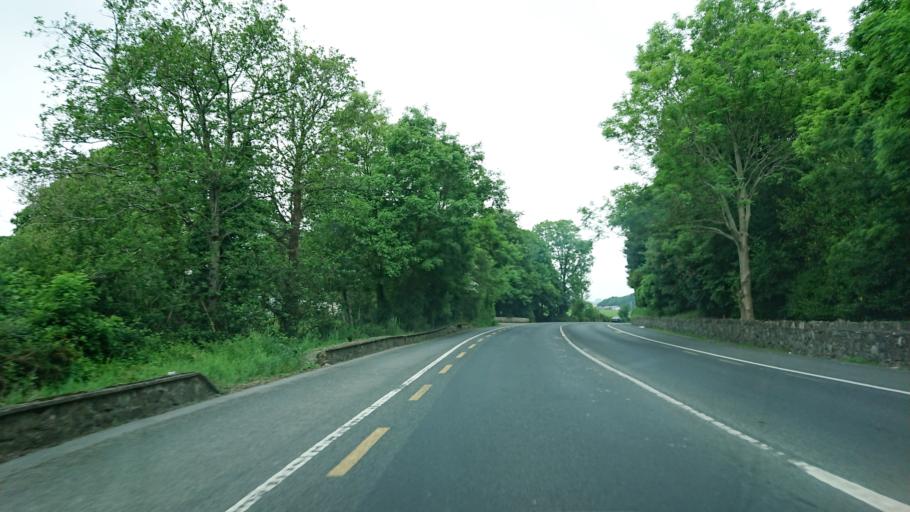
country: IE
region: Munster
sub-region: Waterford
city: Waterford
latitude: 52.2141
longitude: -7.1228
